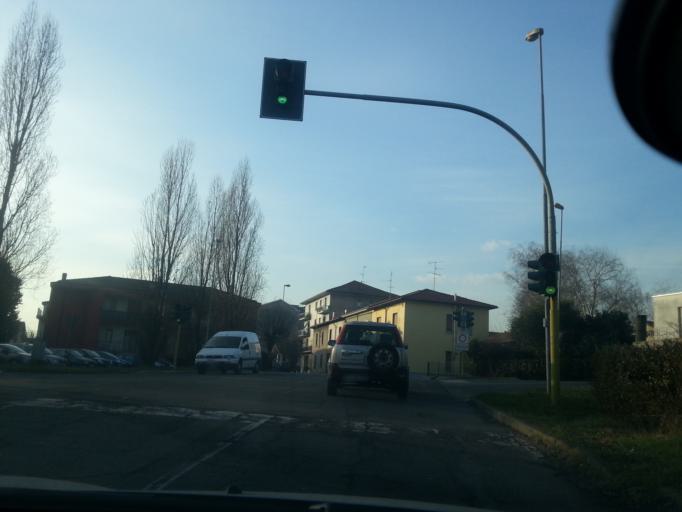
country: IT
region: Lombardy
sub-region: Citta metropolitana di Milano
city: Novate Milanese
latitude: 45.5472
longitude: 9.1473
